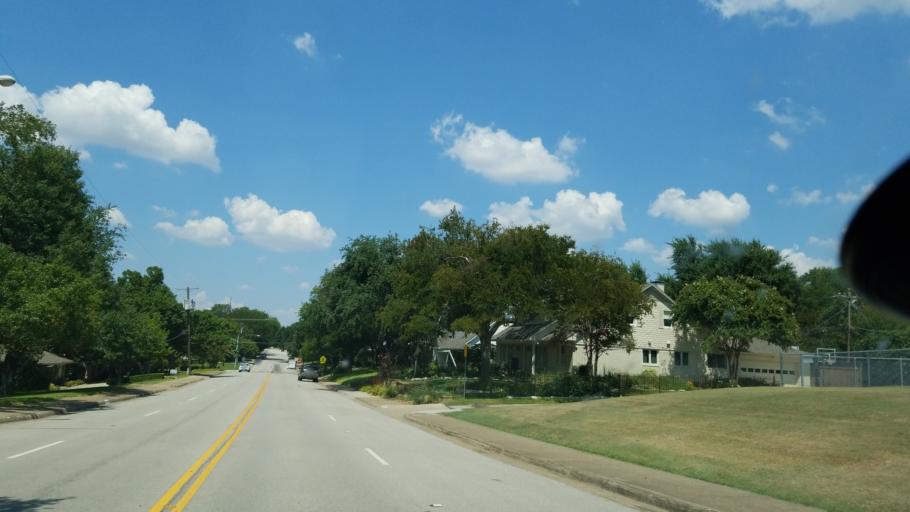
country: US
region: Texas
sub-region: Dallas County
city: Richardson
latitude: 32.8847
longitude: -96.7091
